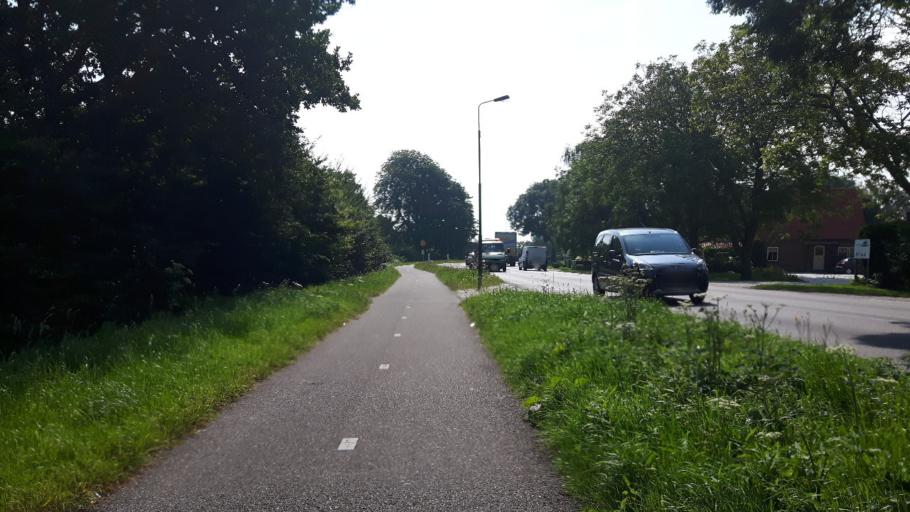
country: NL
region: Utrecht
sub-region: Gemeente Montfoort
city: Montfoort
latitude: 52.0579
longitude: 4.9216
